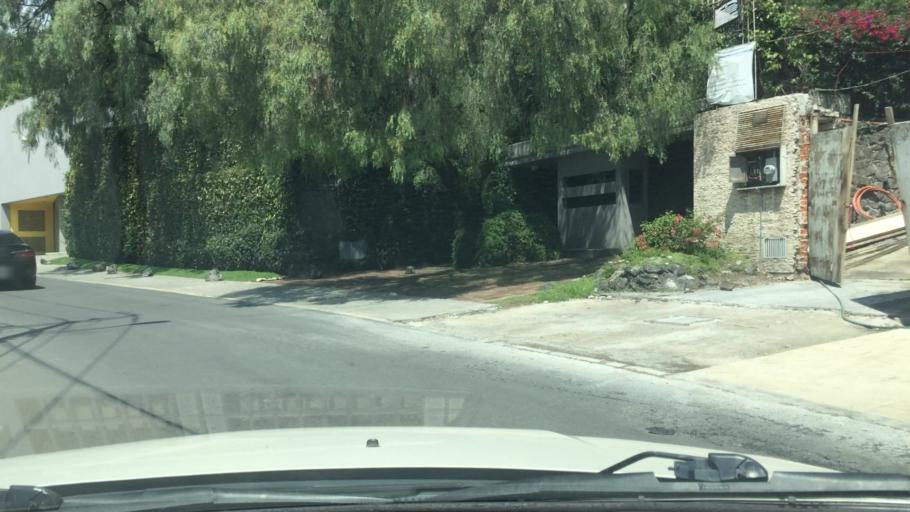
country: MX
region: Mexico City
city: Magdalena Contreras
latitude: 19.3245
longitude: -99.2124
